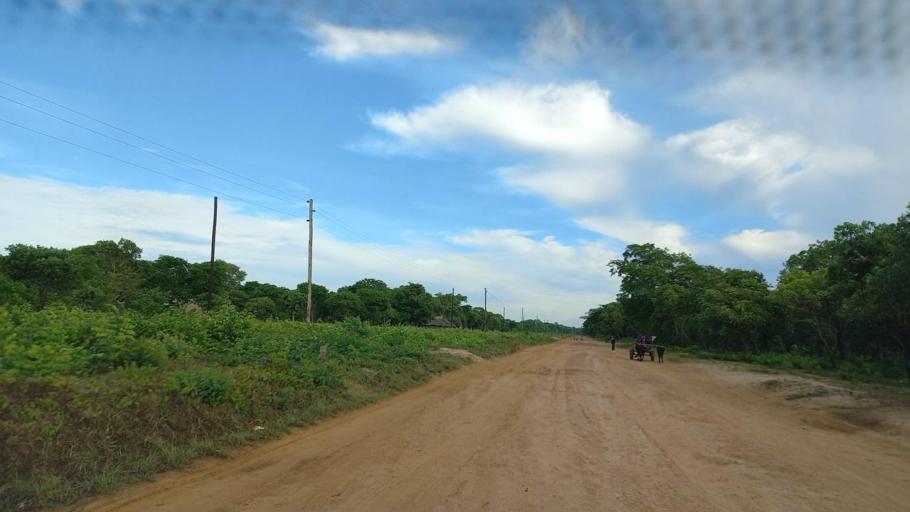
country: ZM
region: North-Western
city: Kabompo
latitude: -13.4102
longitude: 24.3153
